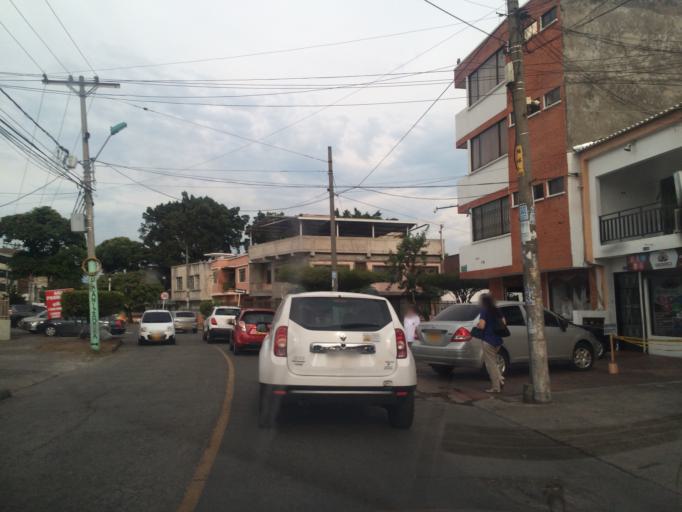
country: CO
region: Valle del Cauca
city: Cali
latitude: 3.4326
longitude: -76.5351
